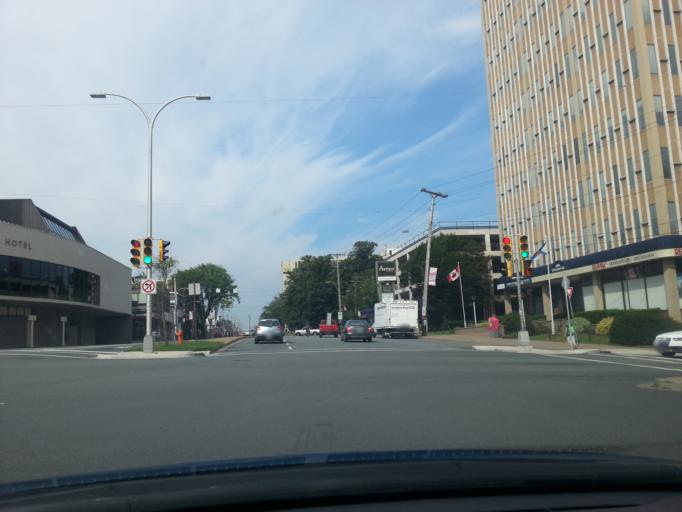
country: CA
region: Nova Scotia
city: Halifax
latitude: 44.6473
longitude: -63.5902
